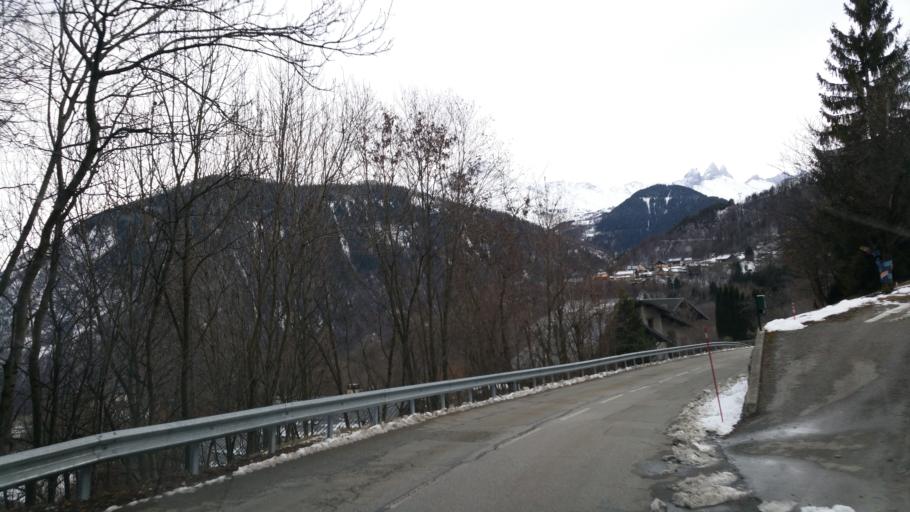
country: FR
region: Rhone-Alpes
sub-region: Departement de la Savoie
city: Saint-Jean-de-Maurienne
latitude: 45.2771
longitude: 6.3232
